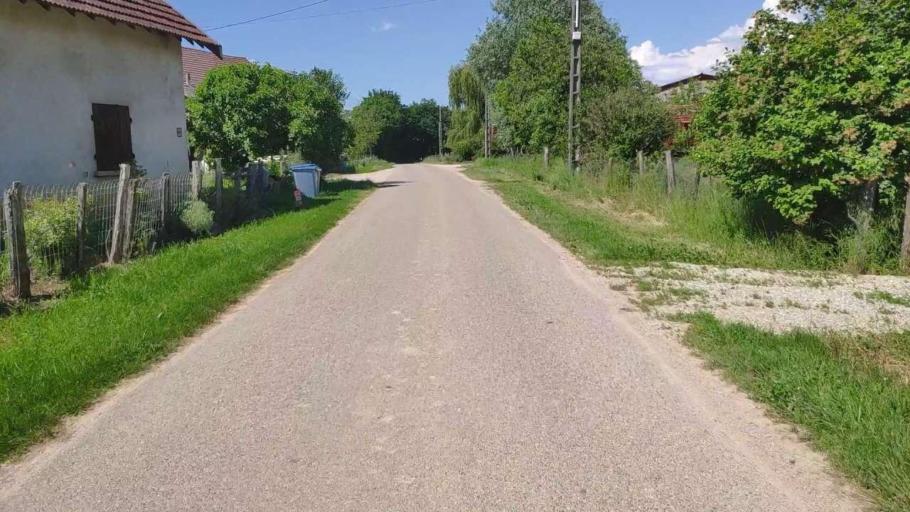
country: FR
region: Franche-Comte
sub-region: Departement du Jura
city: Bletterans
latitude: 46.7982
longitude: 5.4080
